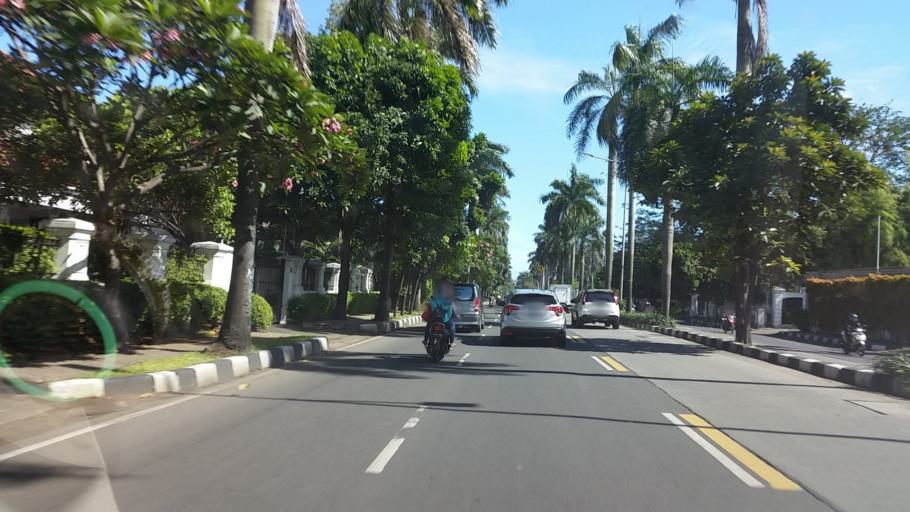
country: ID
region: Banten
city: South Tangerang
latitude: -6.2778
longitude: 106.7815
